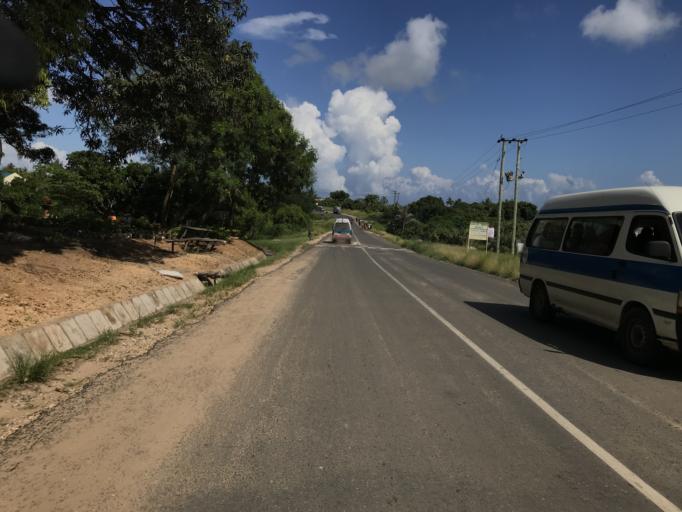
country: TZ
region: Dar es Salaam
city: Dar es Salaam
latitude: -6.8908
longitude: 39.4272
